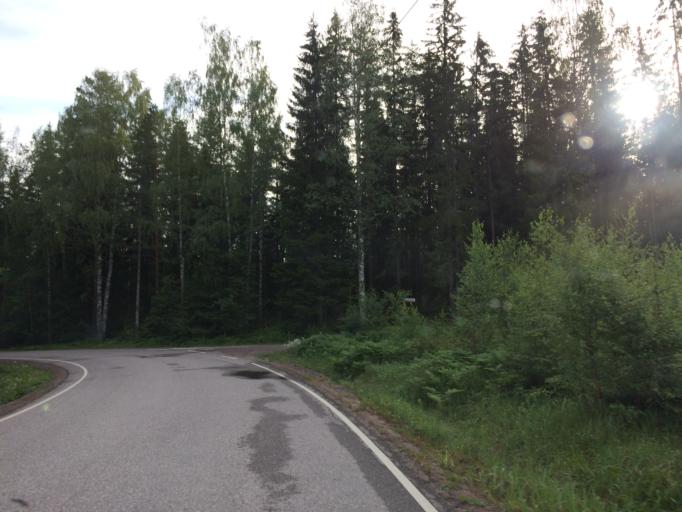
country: FI
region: Haeme
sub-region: Haemeenlinna
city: Janakkala
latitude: 60.8617
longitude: 24.5504
